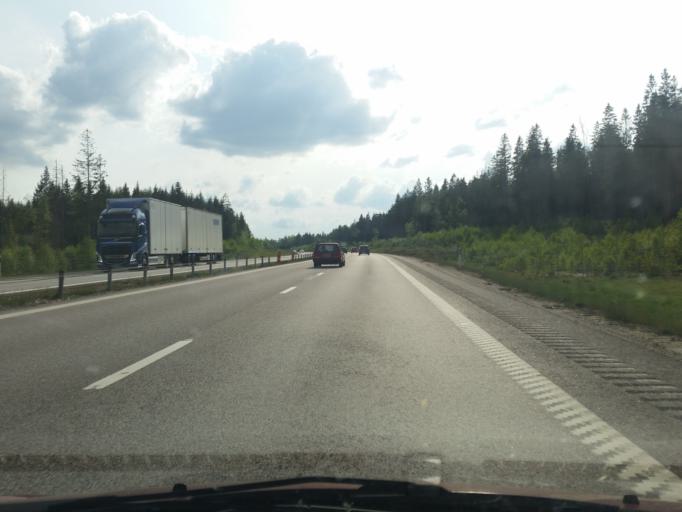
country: SE
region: Vaestra Goetaland
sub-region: Boras Kommun
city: Dalsjofors
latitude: 57.7547
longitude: 13.0862
